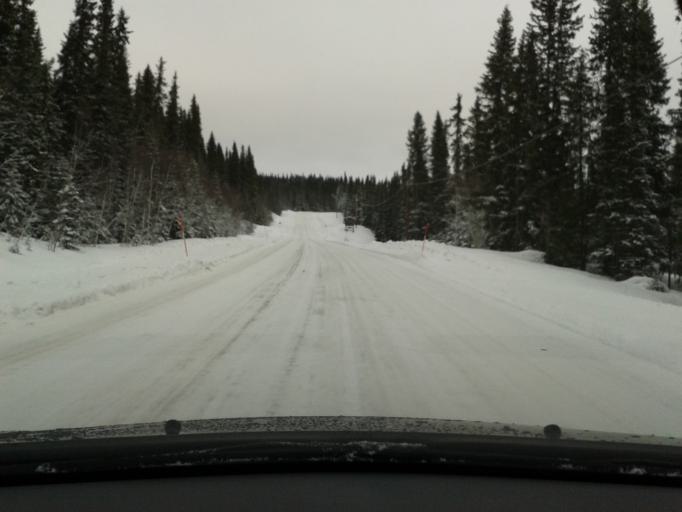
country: SE
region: Vaesterbotten
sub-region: Vilhelmina Kommun
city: Sjoberg
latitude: 65.2298
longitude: 15.9741
